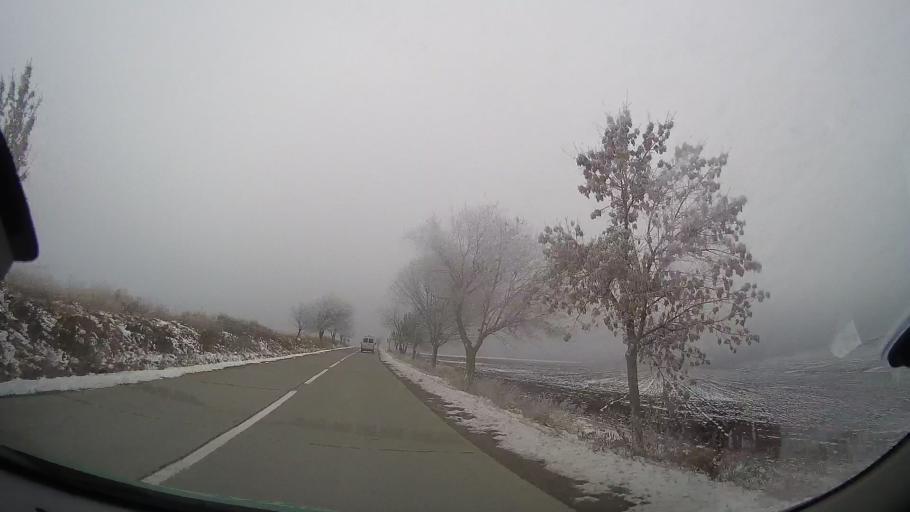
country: RO
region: Vaslui
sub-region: Comuna Ivesti
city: Ivesti
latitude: 46.1969
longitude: 27.5955
